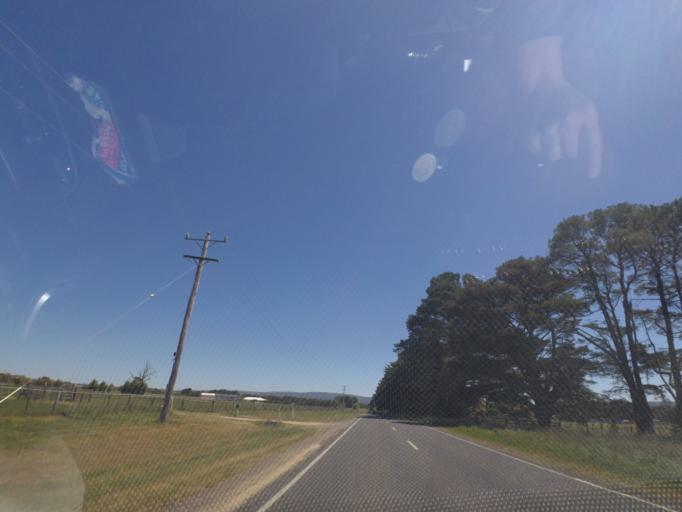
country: AU
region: Victoria
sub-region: Hume
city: Sunbury
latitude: -37.2820
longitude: 144.7520
